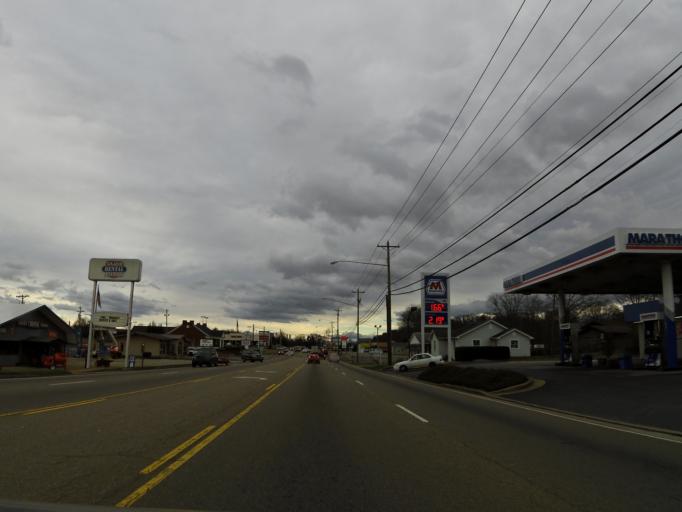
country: US
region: Tennessee
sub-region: Greene County
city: Tusculum
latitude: 36.1781
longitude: -82.7846
